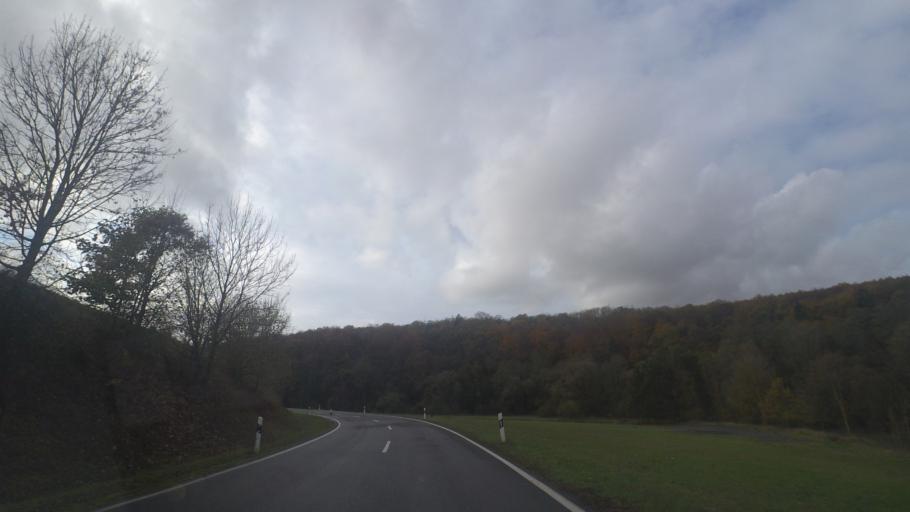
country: DE
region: Bavaria
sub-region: Regierungsbezirk Unterfranken
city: Aubstadt
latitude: 50.3419
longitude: 10.4023
